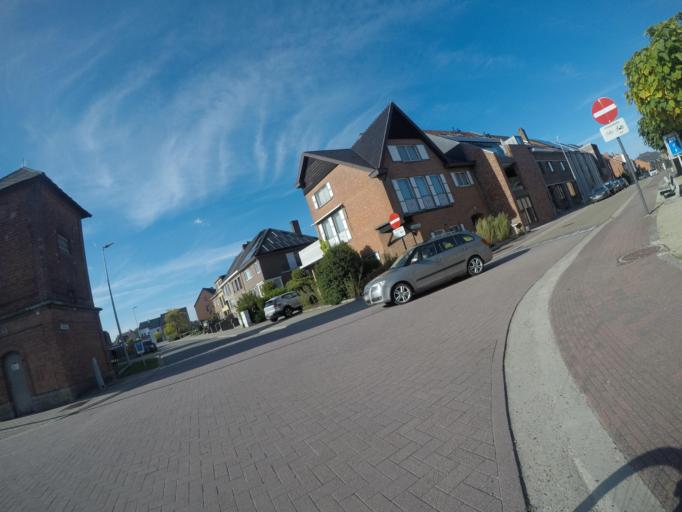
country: BE
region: Flanders
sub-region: Provincie Limburg
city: Diepenbeek
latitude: 50.9075
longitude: 5.4160
